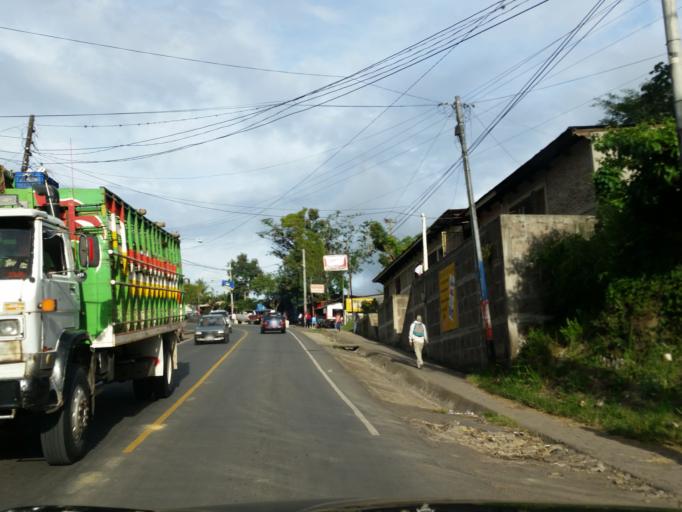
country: NI
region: Matagalpa
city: Matagalpa
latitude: 12.9370
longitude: -85.9087
